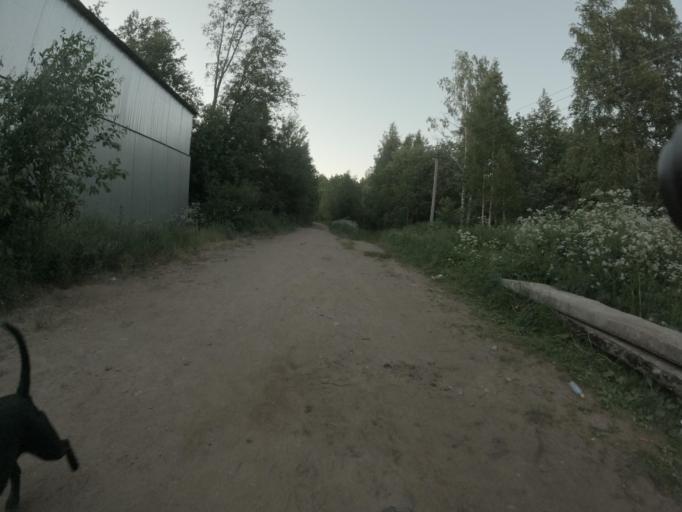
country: RU
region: St.-Petersburg
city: Krasnogvargeisky
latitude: 59.9865
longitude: 30.5301
